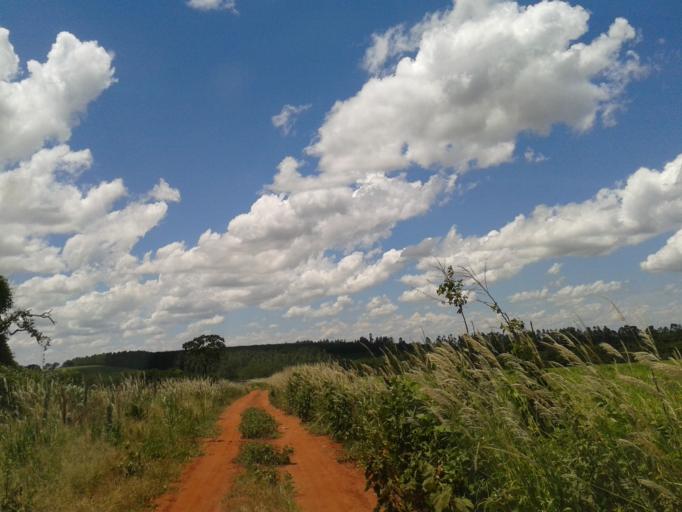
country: BR
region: Minas Gerais
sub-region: Centralina
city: Centralina
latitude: -18.6973
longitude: -49.1646
